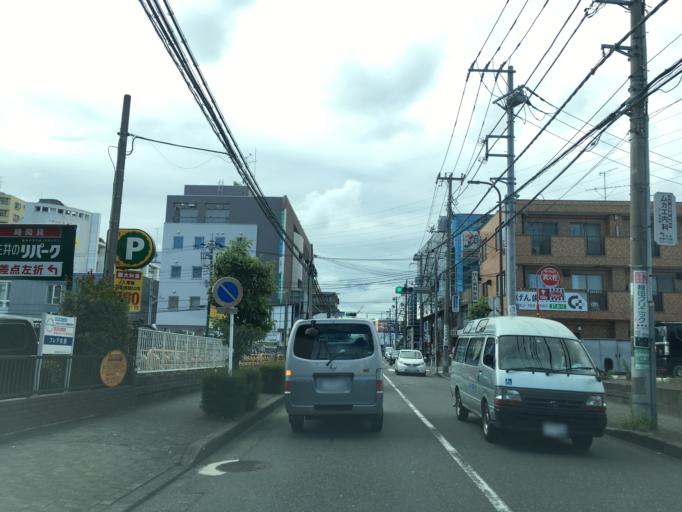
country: JP
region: Tokyo
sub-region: Machida-shi
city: Machida
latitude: 35.5547
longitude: 139.4201
